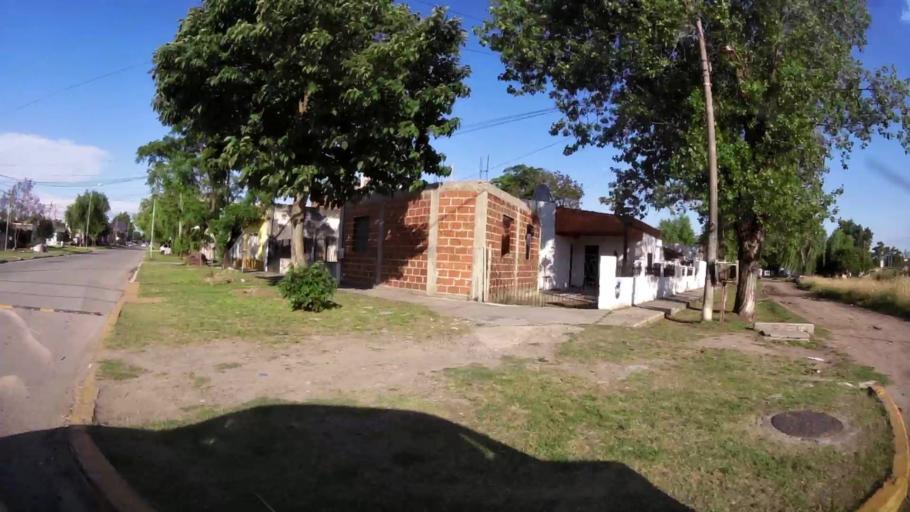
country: AR
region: Buenos Aires
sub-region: Partido de Merlo
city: Merlo
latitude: -34.6815
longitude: -58.7312
